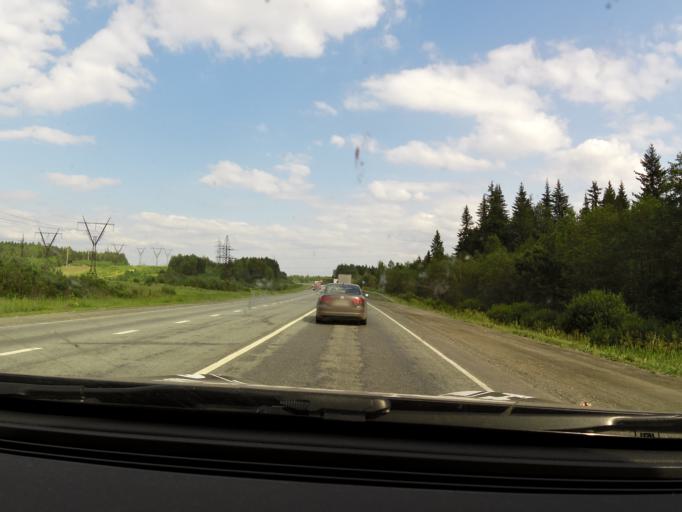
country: RU
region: Sverdlovsk
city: Revda
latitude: 56.8273
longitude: 59.8646
